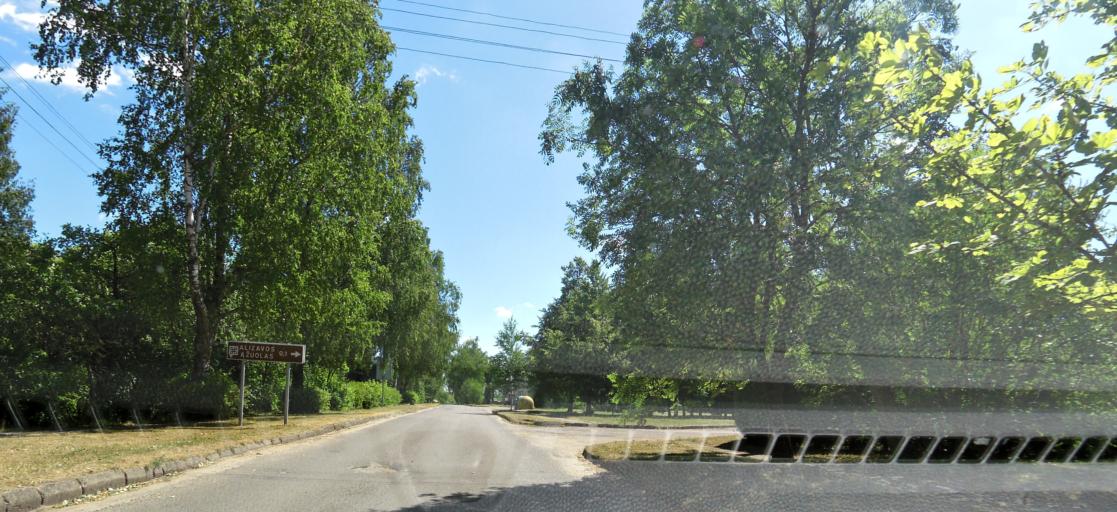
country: LT
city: Kupiskis
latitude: 55.9720
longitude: 24.9987
